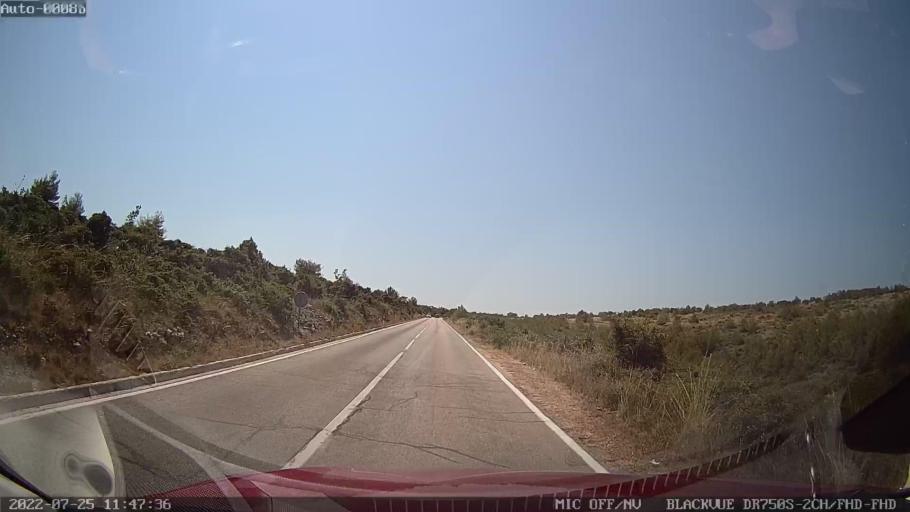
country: HR
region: Zadarska
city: Razanac
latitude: 44.2370
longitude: 15.3023
